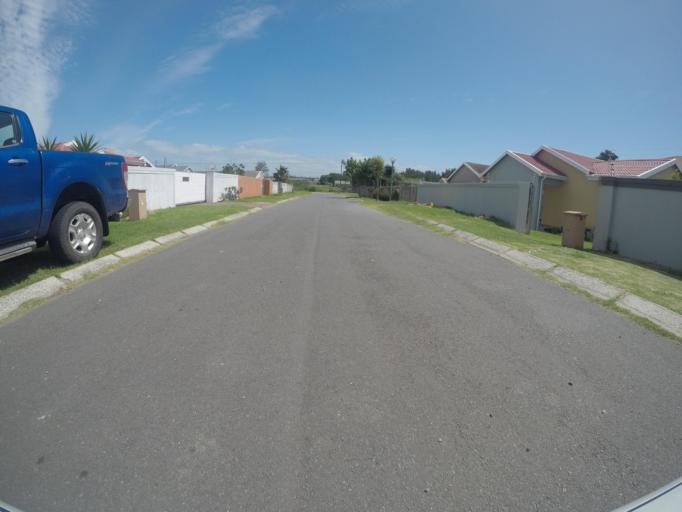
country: ZA
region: Eastern Cape
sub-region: Buffalo City Metropolitan Municipality
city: East London
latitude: -32.9513
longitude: 27.9965
